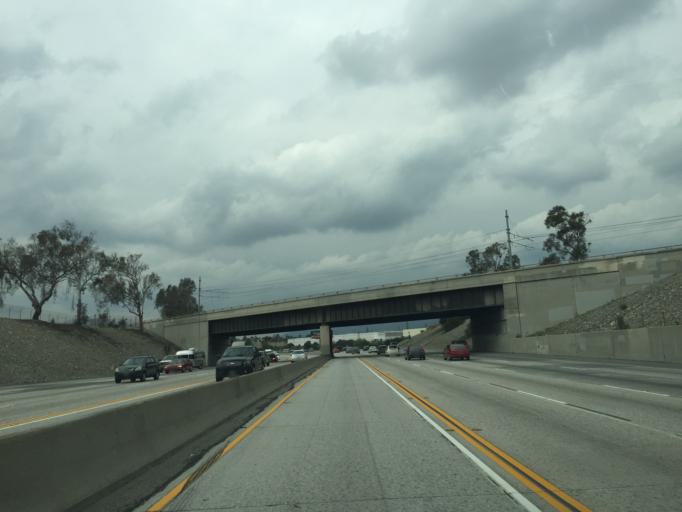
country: US
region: California
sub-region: Los Angeles County
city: Azusa
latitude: 34.1296
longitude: -117.9243
